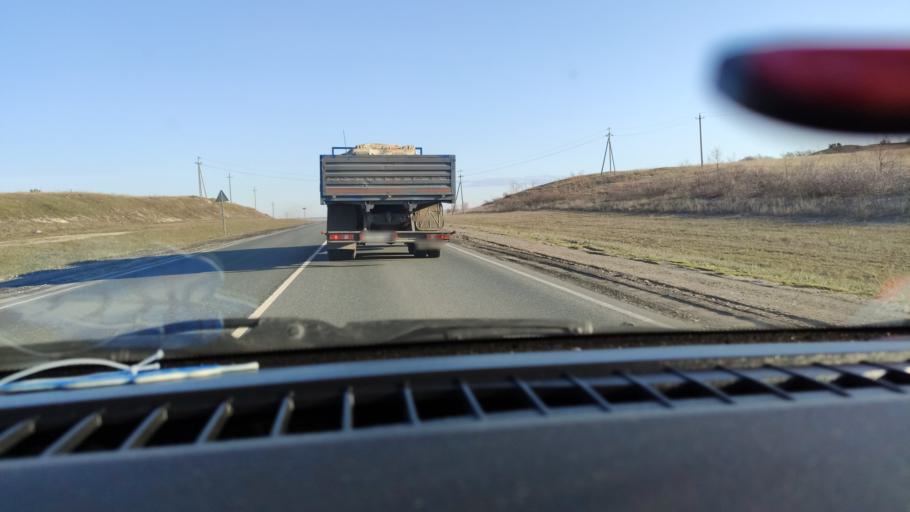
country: RU
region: Saratov
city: Alekseyevka
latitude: 52.3219
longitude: 47.9216
